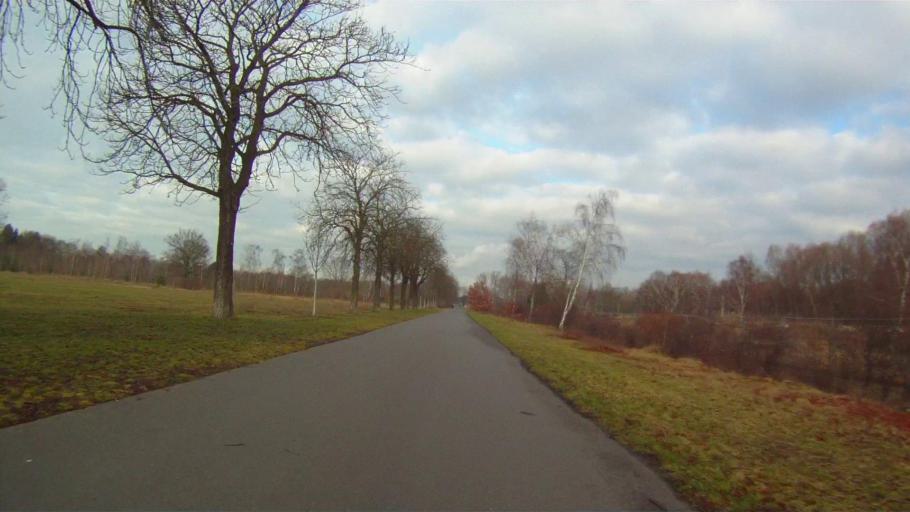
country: DE
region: Berlin
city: Oberschoneweide
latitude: 52.4709
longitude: 13.5250
